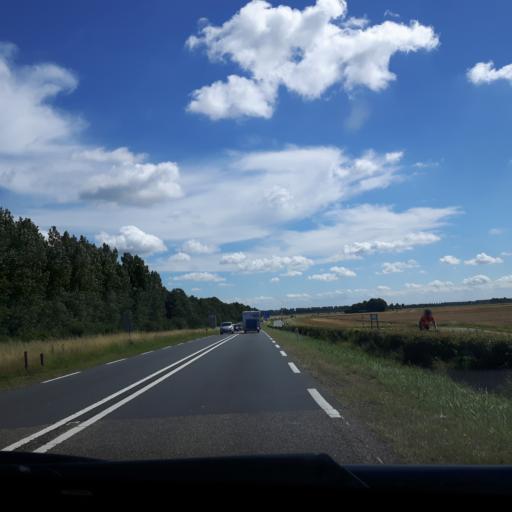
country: NL
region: Zeeland
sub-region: Gemeente Goes
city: Goes
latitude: 51.5391
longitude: 3.8670
